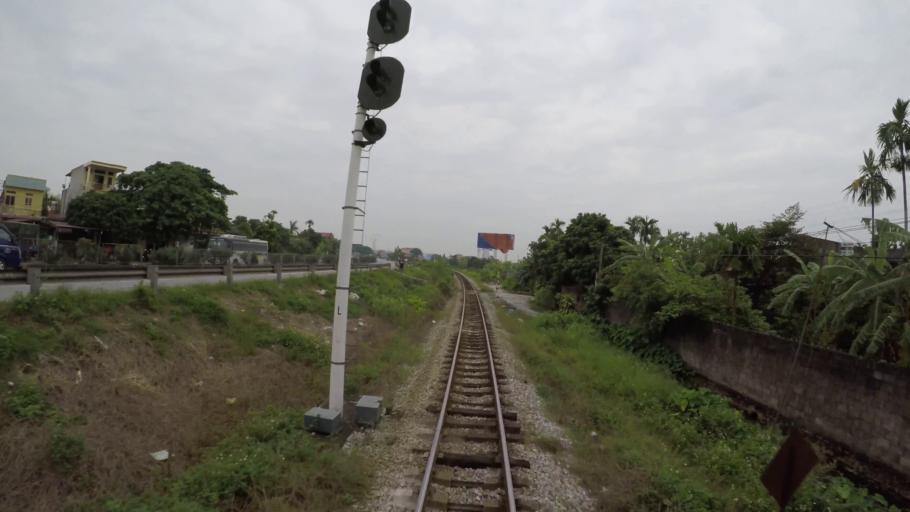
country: VN
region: Hai Duong
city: Phu Thai
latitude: 20.9347
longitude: 106.5506
